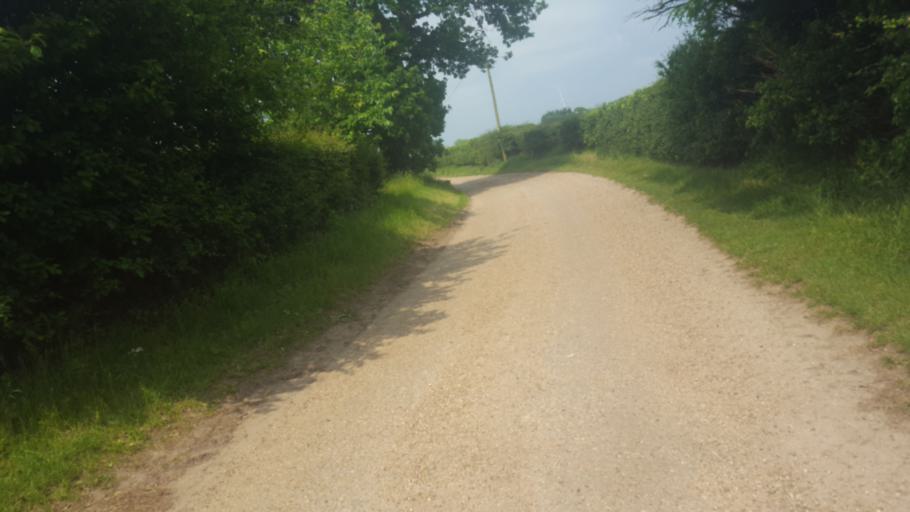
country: GB
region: England
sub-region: Essex
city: Saint Osyth
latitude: 51.7977
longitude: 1.0996
